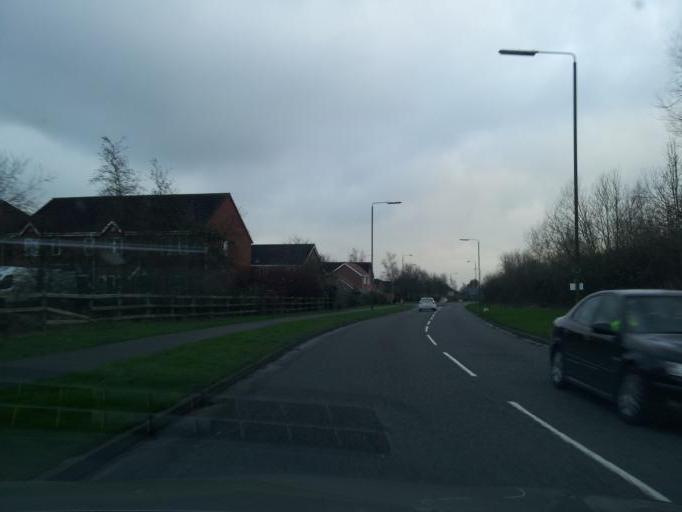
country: GB
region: England
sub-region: Derbyshire
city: Etwall
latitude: 52.8751
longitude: -1.6285
